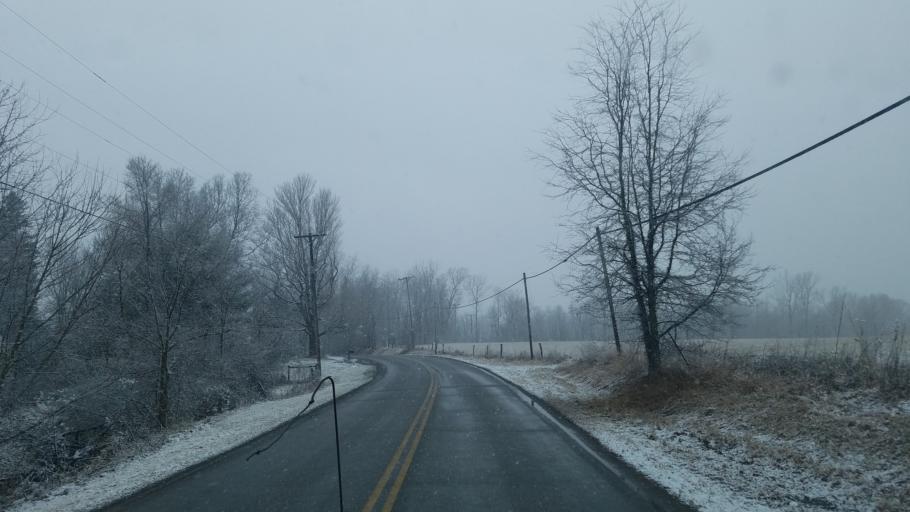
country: US
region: Ohio
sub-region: Logan County
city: Bellefontaine
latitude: 40.3341
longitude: -83.6717
